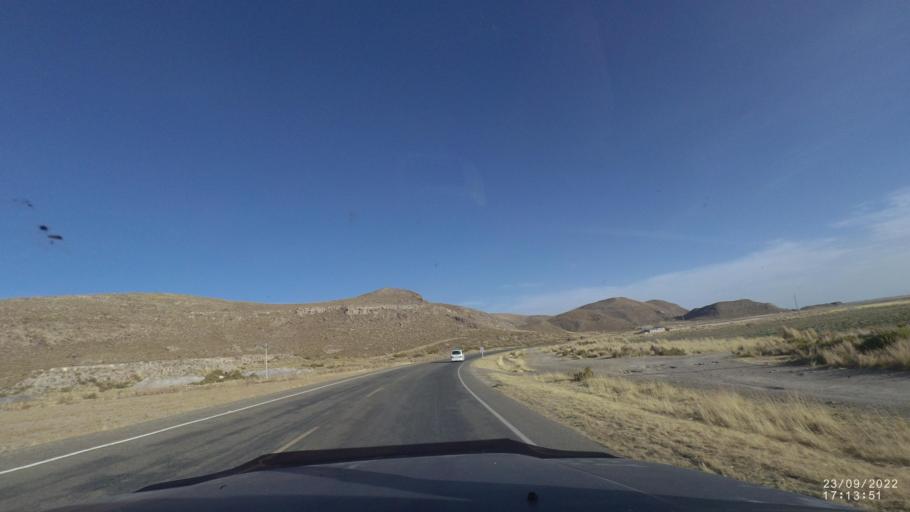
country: BO
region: Oruro
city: Challapata
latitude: -18.7143
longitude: -66.8701
